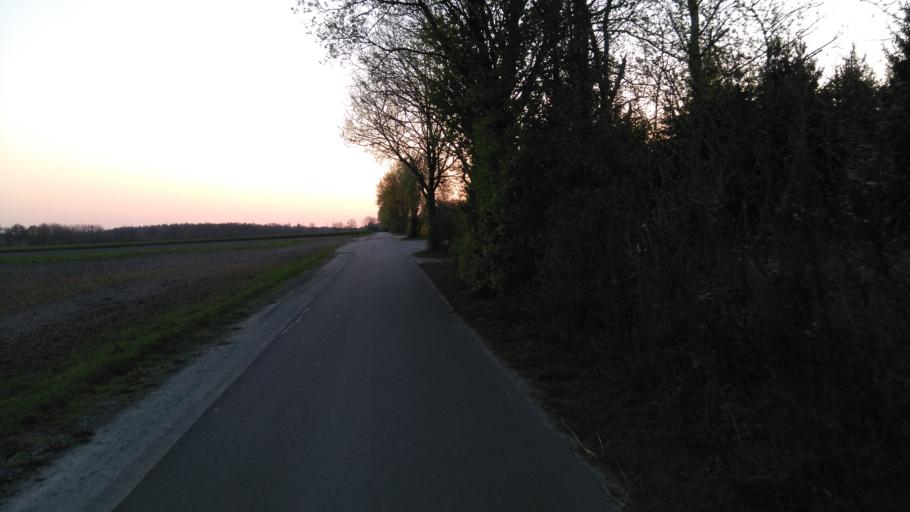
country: DE
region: Lower Saxony
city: Bargstedt
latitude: 53.4481
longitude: 9.4652
